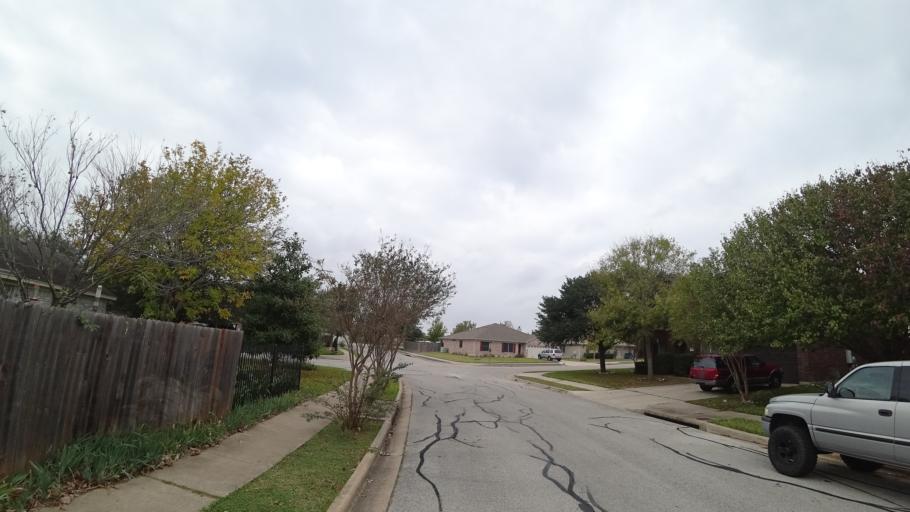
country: US
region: Texas
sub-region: Travis County
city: Pflugerville
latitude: 30.4376
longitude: -97.6085
